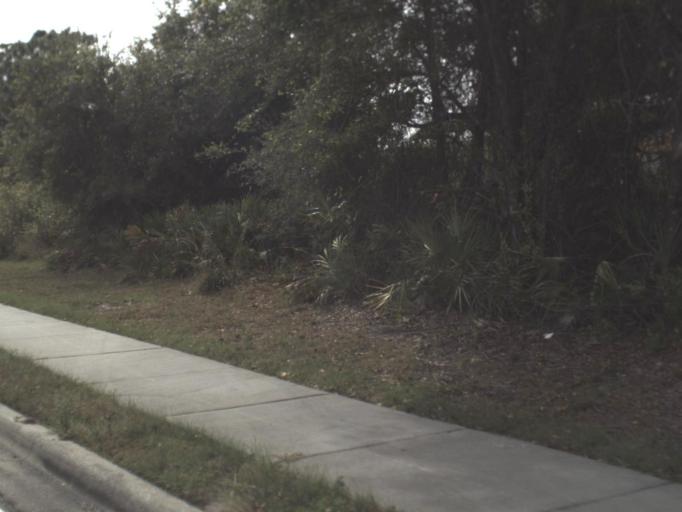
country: US
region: Florida
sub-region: Orange County
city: Belle Isle
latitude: 28.4417
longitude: -81.3470
